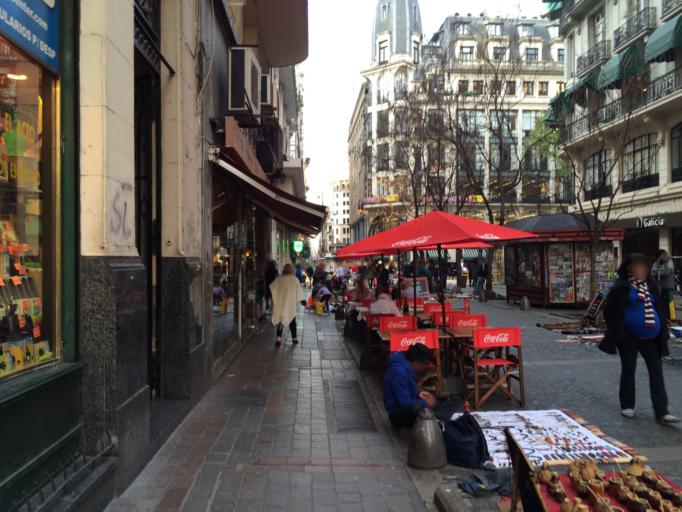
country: AR
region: Buenos Aires F.D.
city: Buenos Aires
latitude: -34.6092
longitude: -58.3749
